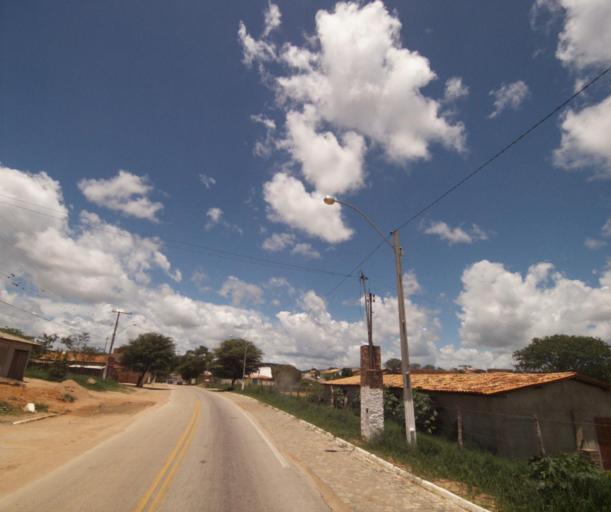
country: BR
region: Bahia
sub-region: Pocoes
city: Pocoes
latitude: -14.3786
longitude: -40.5079
